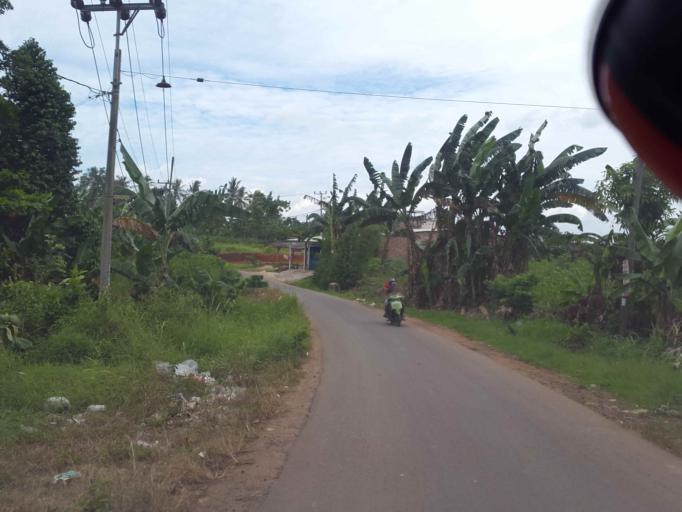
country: ID
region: Lampung
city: Kedaton
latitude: -5.3479
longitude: 105.2317
